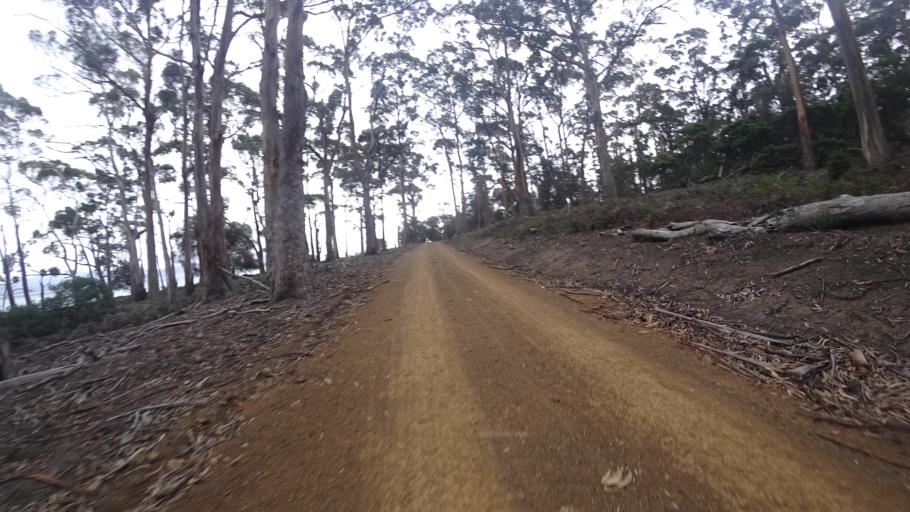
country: AU
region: Tasmania
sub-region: Sorell
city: Sorell
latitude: -42.6183
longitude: 148.0386
